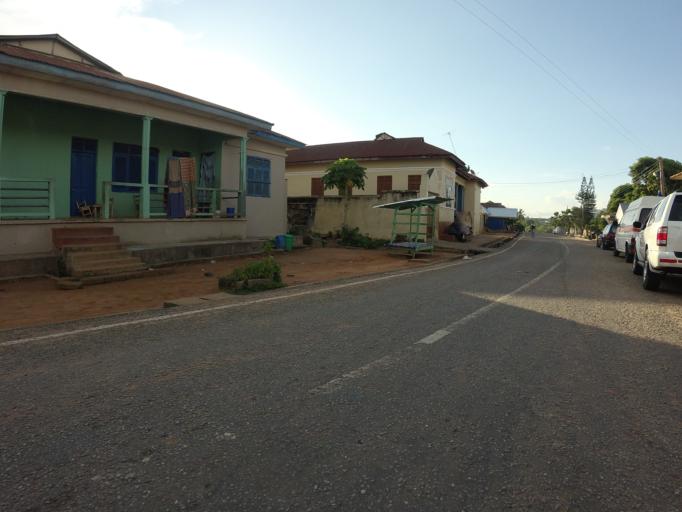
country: GH
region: Ashanti
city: Tafo
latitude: 6.9402
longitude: -1.6747
